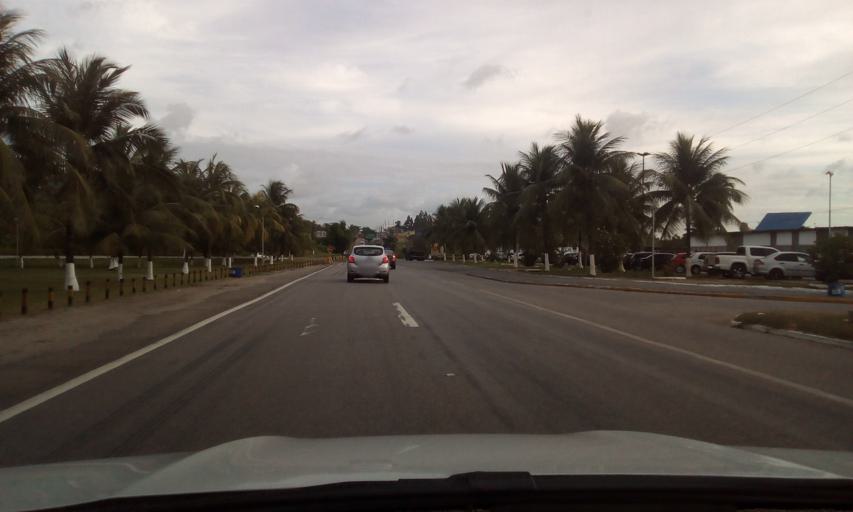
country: BR
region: Pernambuco
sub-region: Igarassu
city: Igarassu
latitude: -7.8333
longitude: -34.9135
